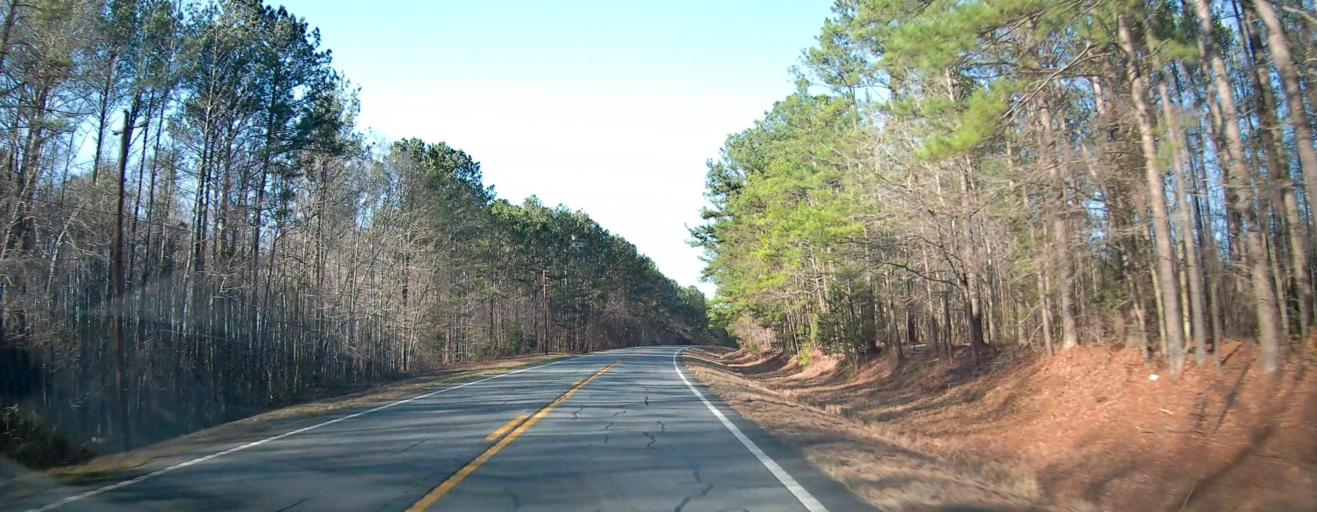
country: US
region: Georgia
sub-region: Talbot County
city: Talbotton
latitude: 32.7156
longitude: -84.5568
